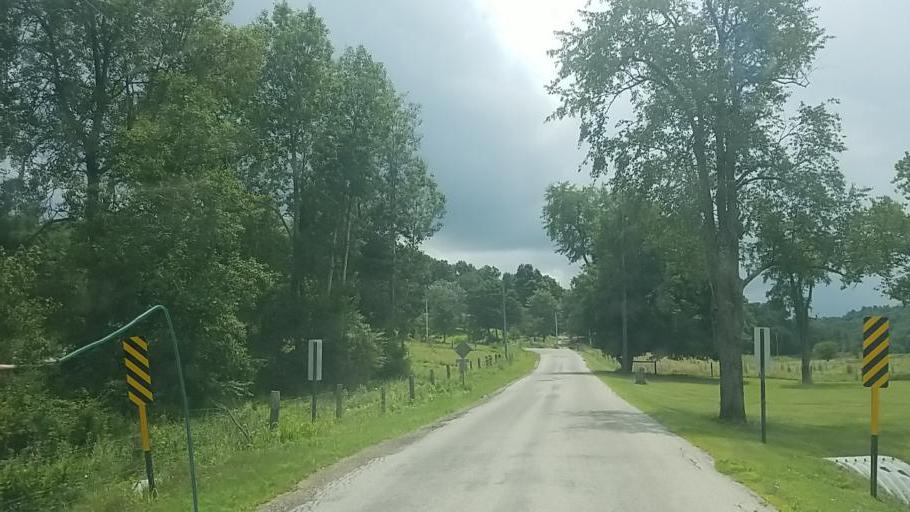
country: US
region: Ohio
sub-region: Muskingum County
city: Frazeysburg
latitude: 40.1976
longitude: -82.2624
